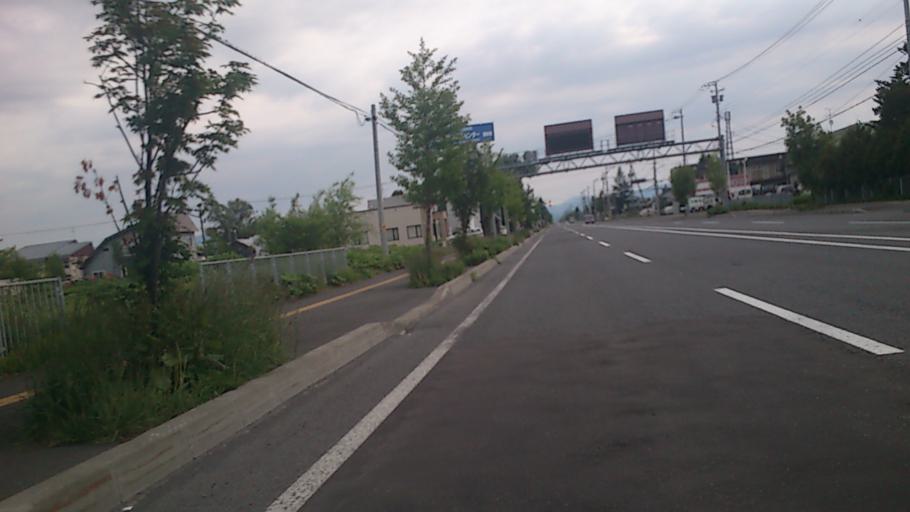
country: JP
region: Hokkaido
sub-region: Asahikawa-shi
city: Asahikawa
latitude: 43.8183
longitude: 142.4462
